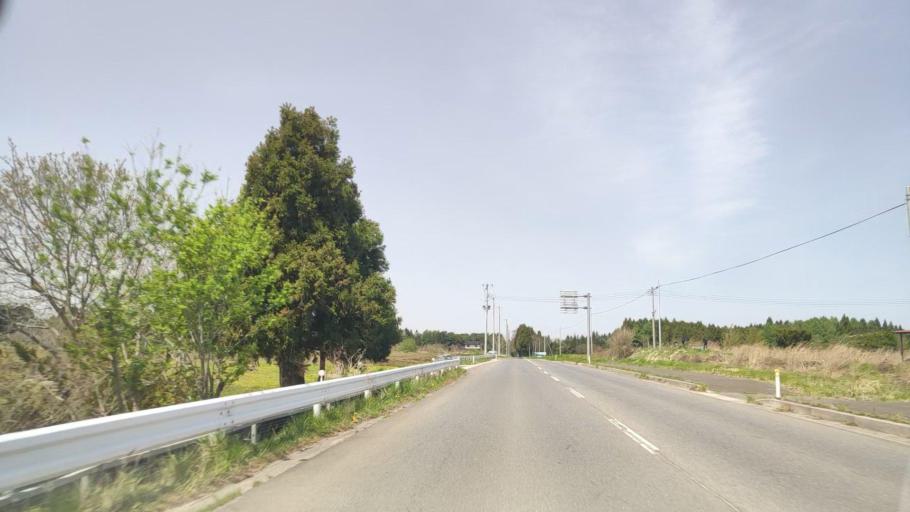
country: JP
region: Aomori
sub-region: Hachinohe Shi
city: Uchimaru
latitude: 40.5291
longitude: 141.4072
